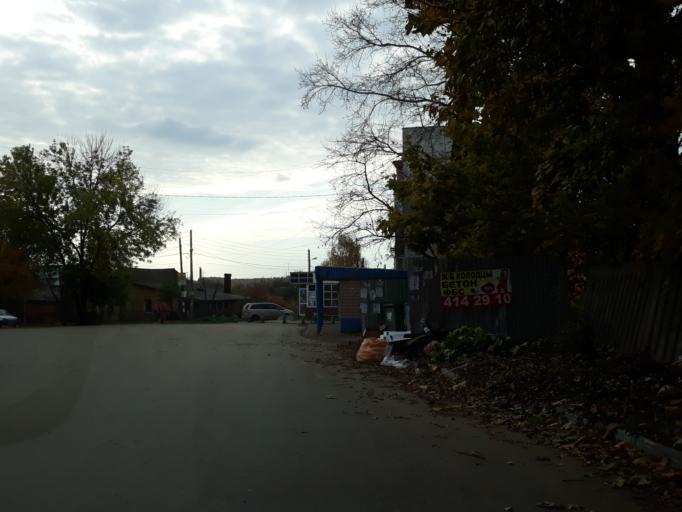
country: RU
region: Nizjnij Novgorod
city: Nizhniy Novgorod
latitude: 56.2344
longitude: 43.9779
